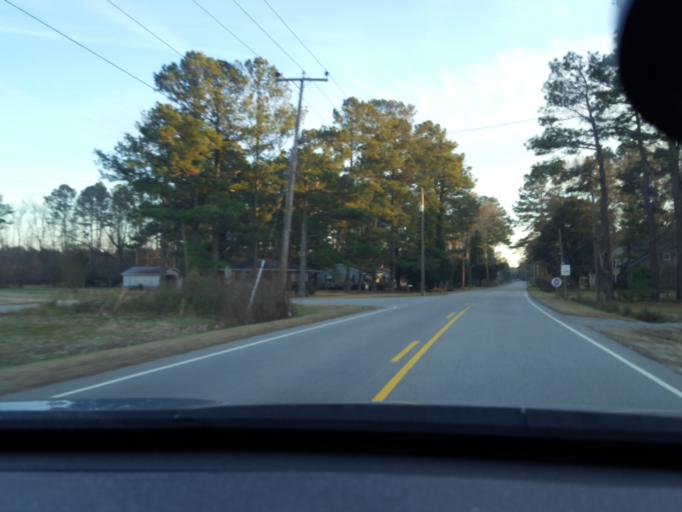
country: US
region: North Carolina
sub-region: Hertford County
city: Ahoskie
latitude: 36.2384
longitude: -77.1166
